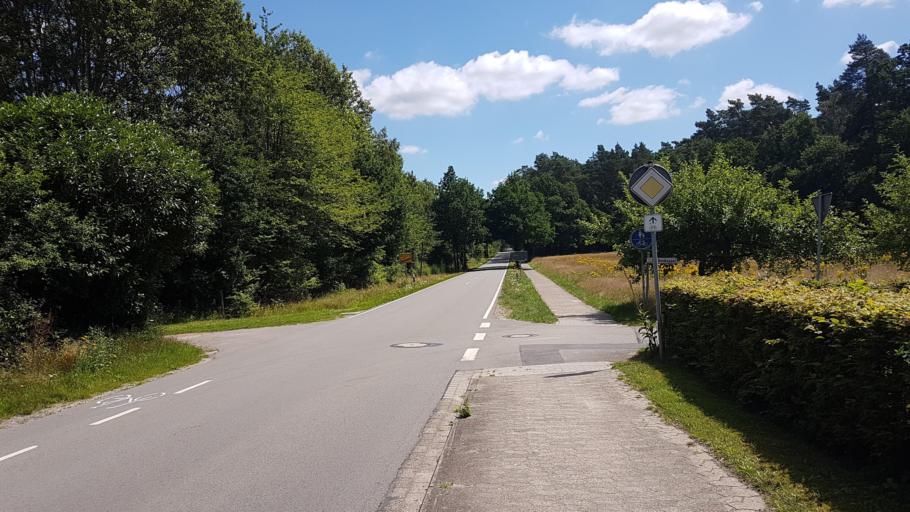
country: DE
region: Lower Saxony
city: Rullstorf
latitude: 53.2826
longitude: 10.5388
